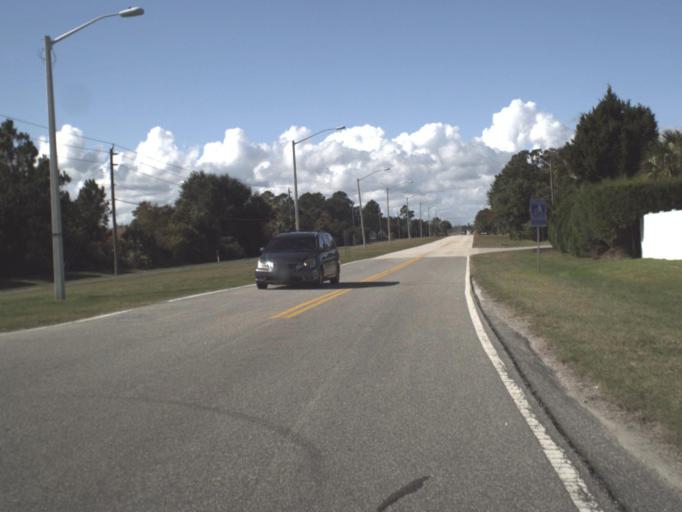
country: US
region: Florida
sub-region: Flagler County
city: Palm Coast
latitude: 29.5986
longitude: -81.2525
